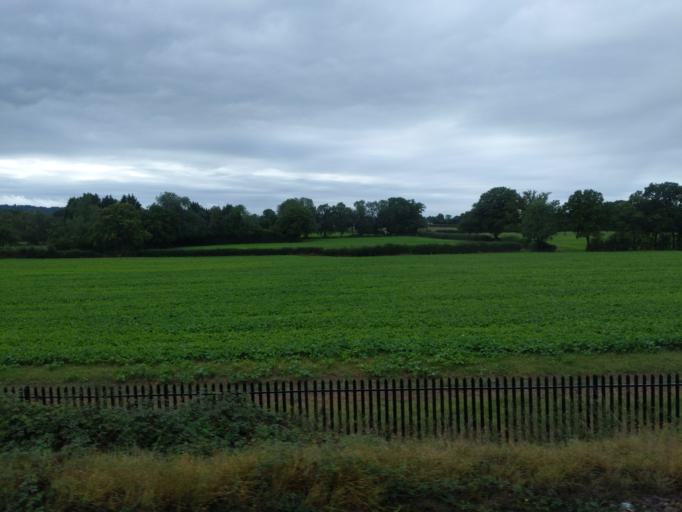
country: GB
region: England
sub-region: Kent
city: Tonbridge
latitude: 51.2090
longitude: 0.2430
